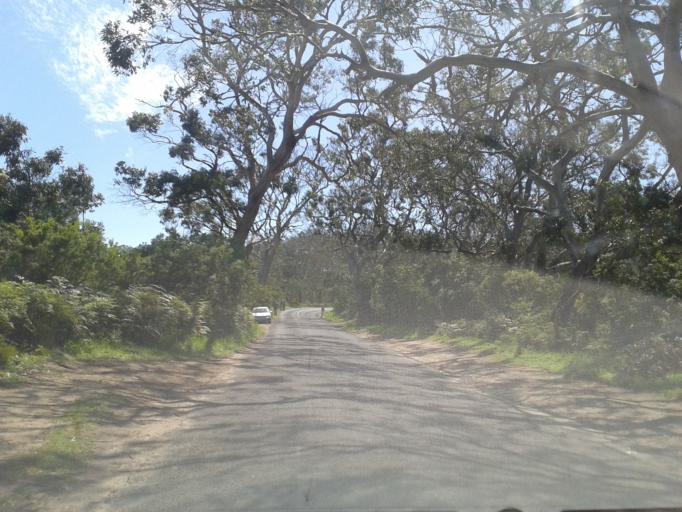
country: AU
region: Victoria
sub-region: Colac-Otway
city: Apollo Bay
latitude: -38.8319
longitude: 143.5201
